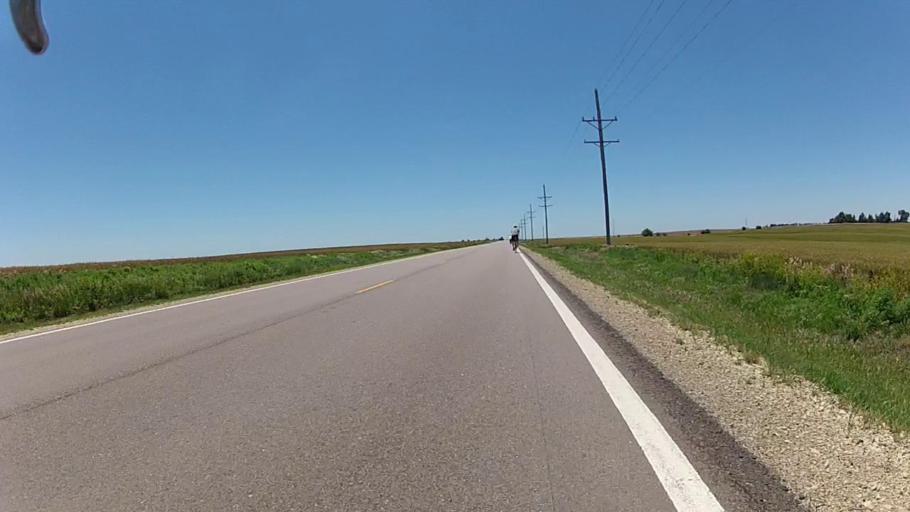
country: US
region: Kansas
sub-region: Kiowa County
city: Greensburg
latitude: 37.5305
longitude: -99.3206
